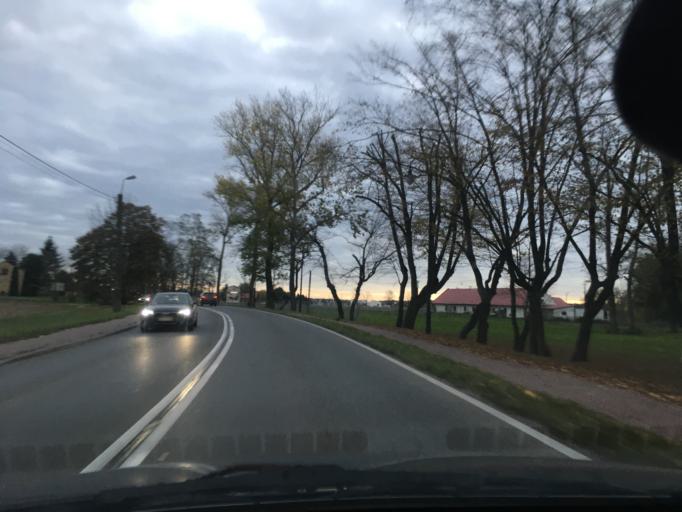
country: PL
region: Masovian Voivodeship
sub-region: Powiat piaseczynski
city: Lesznowola
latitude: 52.0882
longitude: 20.9370
